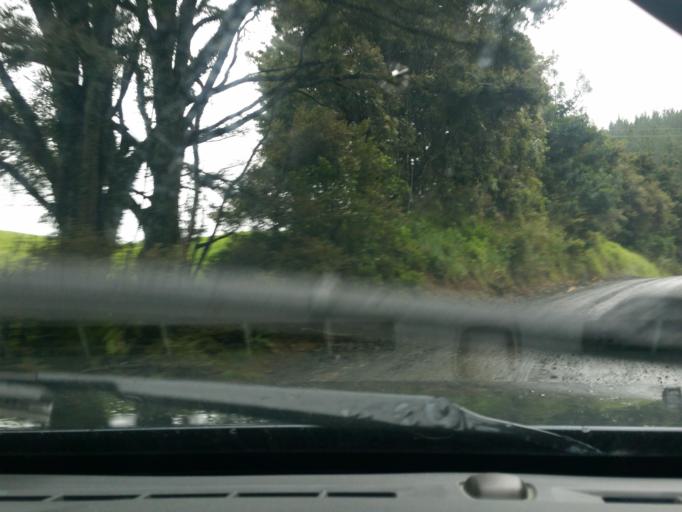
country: NZ
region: Northland
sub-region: Kaipara District
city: Dargaville
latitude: -35.8313
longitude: 173.8242
